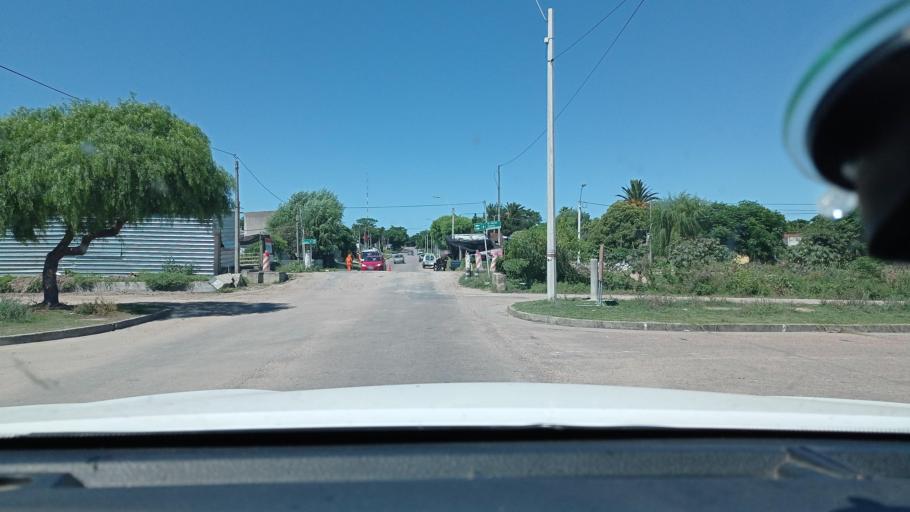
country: UY
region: Canelones
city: Las Piedras
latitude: -34.7365
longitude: -56.2212
